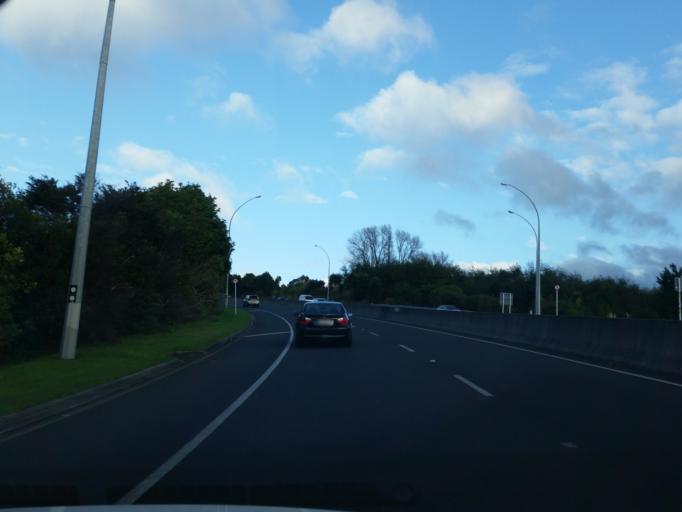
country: NZ
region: Bay of Plenty
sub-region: Tauranga City
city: Tauranga
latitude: -37.6981
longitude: 176.1280
